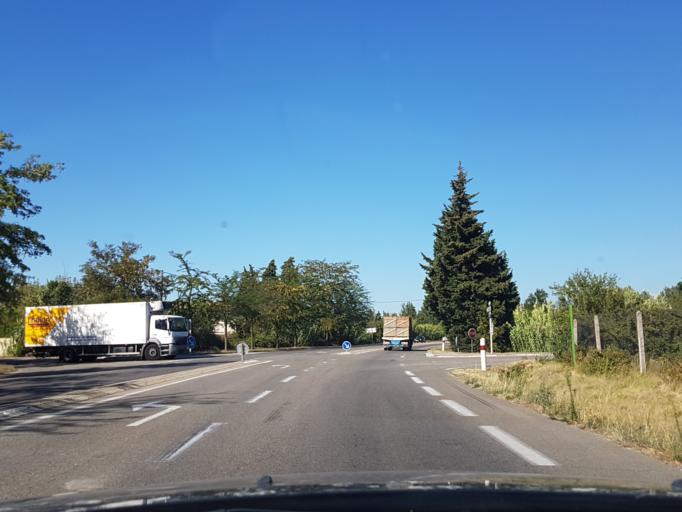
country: FR
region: Provence-Alpes-Cote d'Azur
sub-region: Departement du Vaucluse
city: L'Isle-sur-la-Sorgue
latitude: 43.9254
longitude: 5.0284
